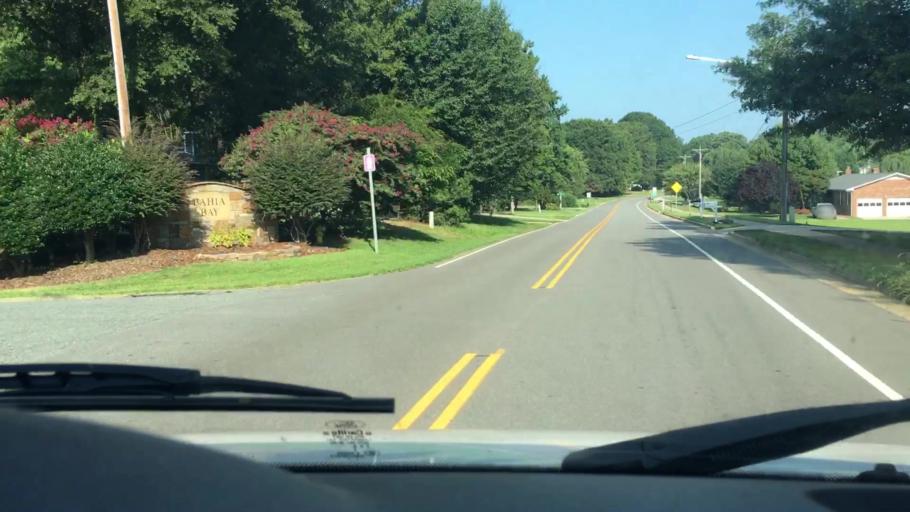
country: US
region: North Carolina
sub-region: Mecklenburg County
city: Cornelius
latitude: 35.4991
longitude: -80.8858
